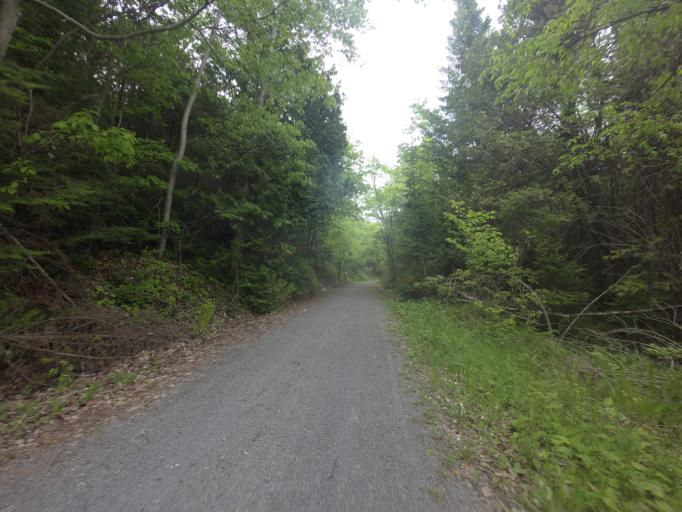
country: CA
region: Ontario
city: Kingston
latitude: 44.3874
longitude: -76.6422
